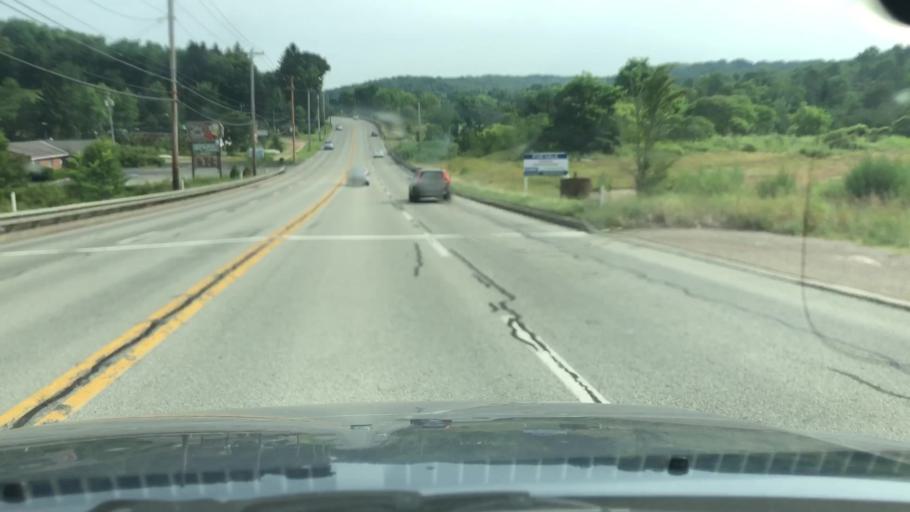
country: US
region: Pennsylvania
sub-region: Allegheny County
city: Bakerstown
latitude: 40.6680
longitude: -79.9333
